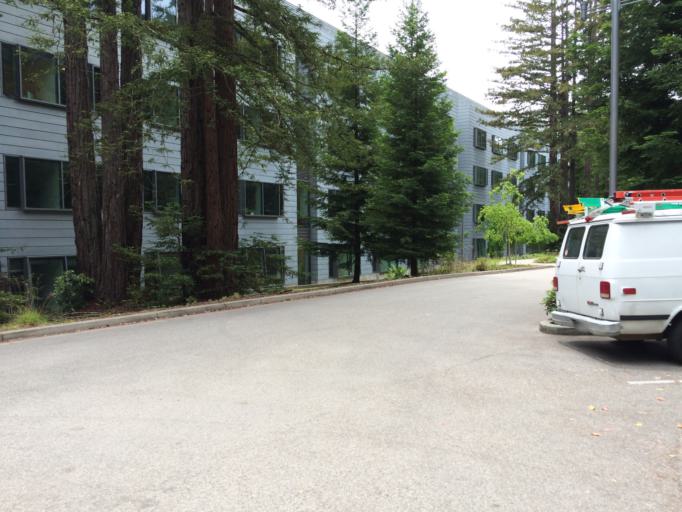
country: US
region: California
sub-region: Santa Cruz County
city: Pasatiempo
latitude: 37.0015
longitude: -122.0624
